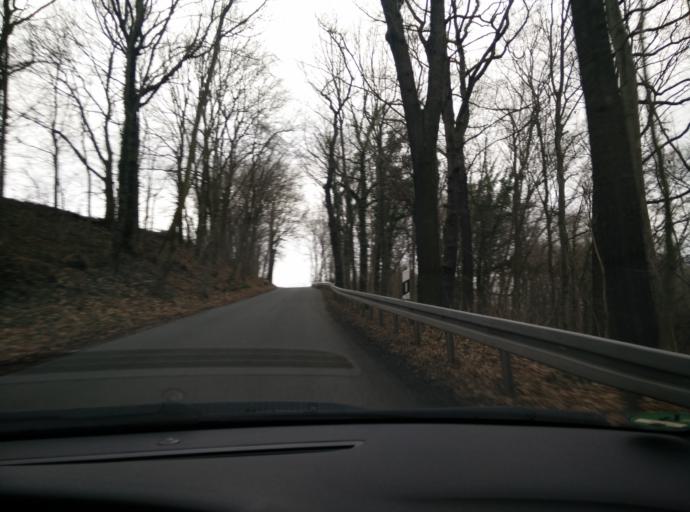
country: DE
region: Saxony
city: Frohburg
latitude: 51.0175
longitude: 12.5961
